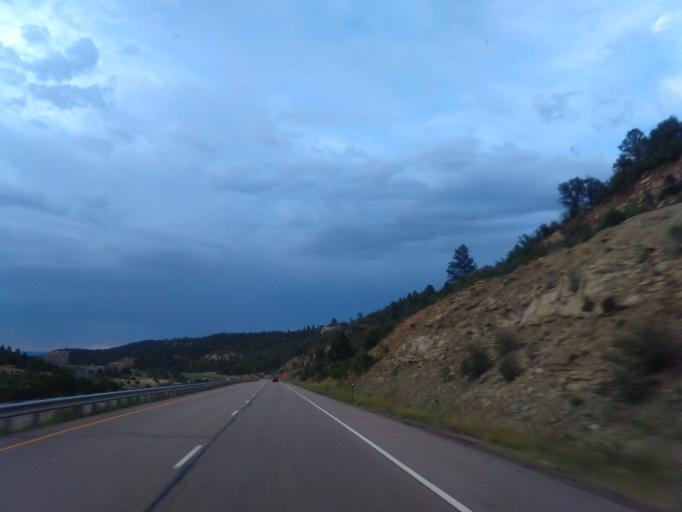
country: US
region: Colorado
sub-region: Las Animas County
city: Trinidad
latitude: 37.0669
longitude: -104.5186
